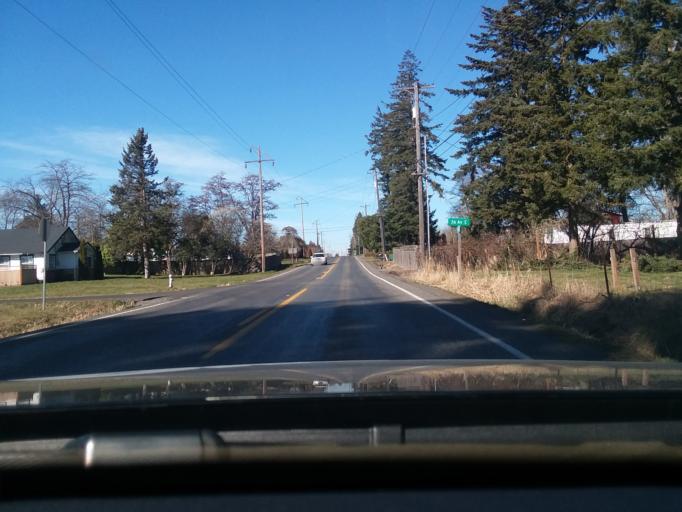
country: US
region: Washington
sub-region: Pierce County
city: Midland
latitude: 47.1622
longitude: -122.3944
